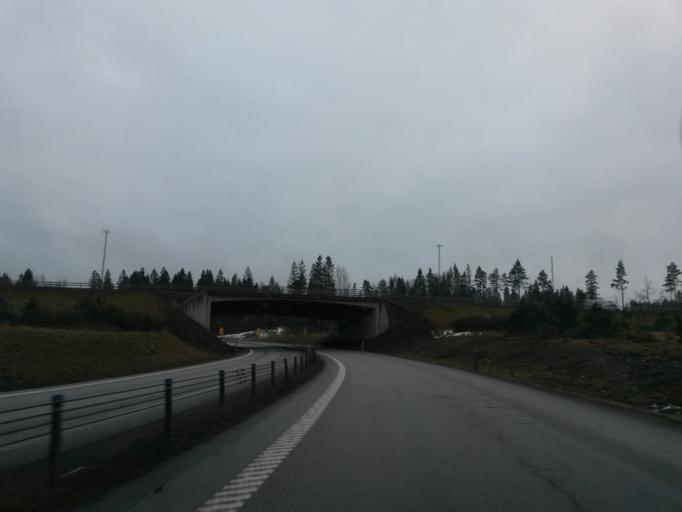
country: SE
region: Vaestra Goetaland
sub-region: Uddevalla Kommun
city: Uddevalla
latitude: 58.3368
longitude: 11.9858
